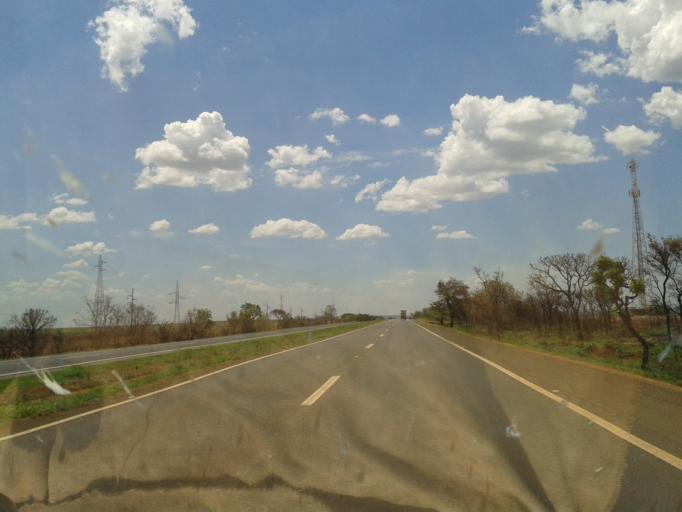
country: BR
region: Minas Gerais
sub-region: Uberlandia
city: Uberlandia
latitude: -19.0719
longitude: -48.1898
